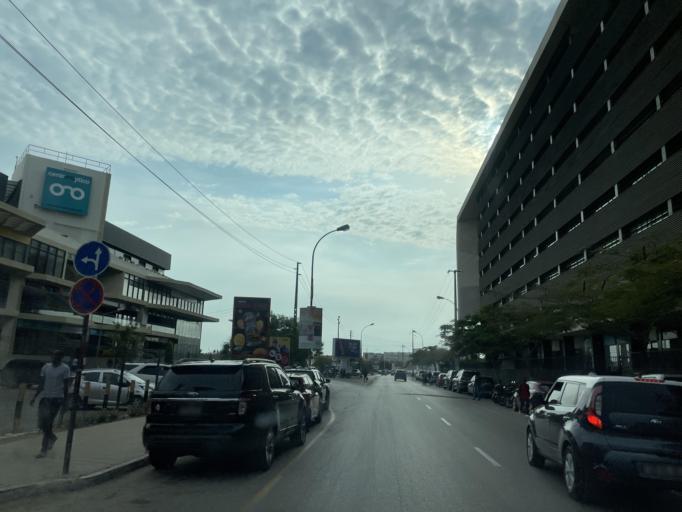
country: AO
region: Luanda
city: Luanda
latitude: -8.9189
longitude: 13.1859
